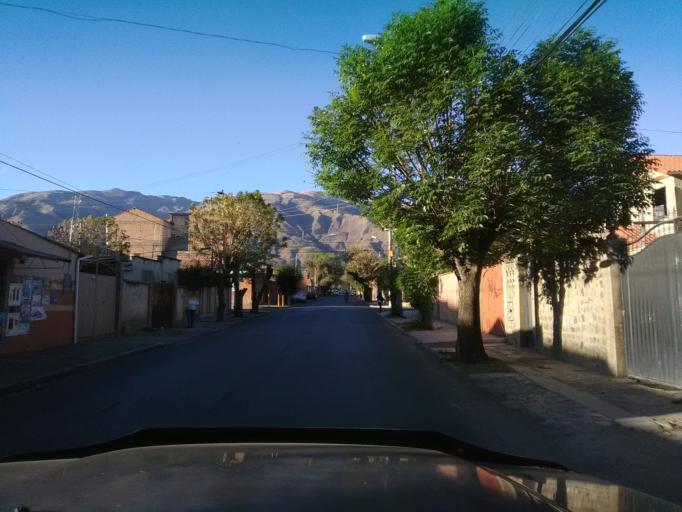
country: BO
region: Cochabamba
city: Cochabamba
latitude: -17.3654
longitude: -66.1873
